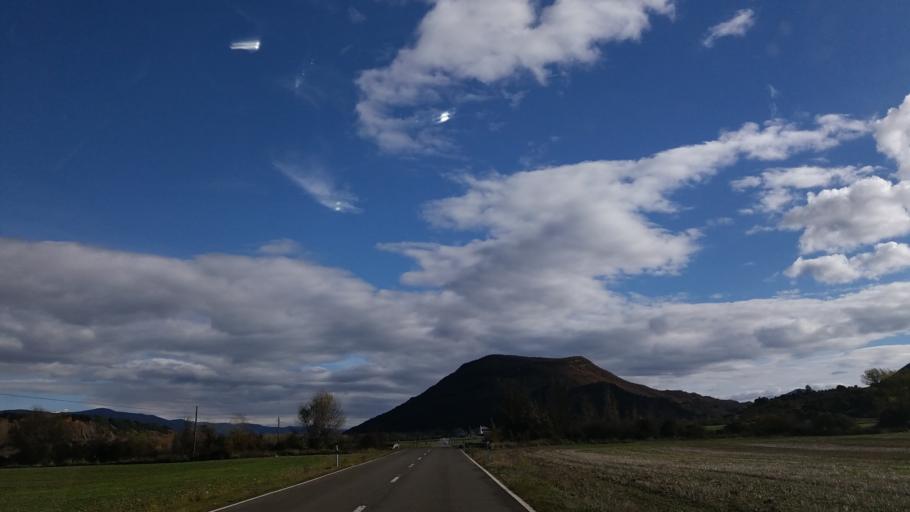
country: ES
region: Aragon
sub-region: Provincia de Huesca
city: Santa Cruz de la Seros
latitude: 42.5561
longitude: -0.6921
